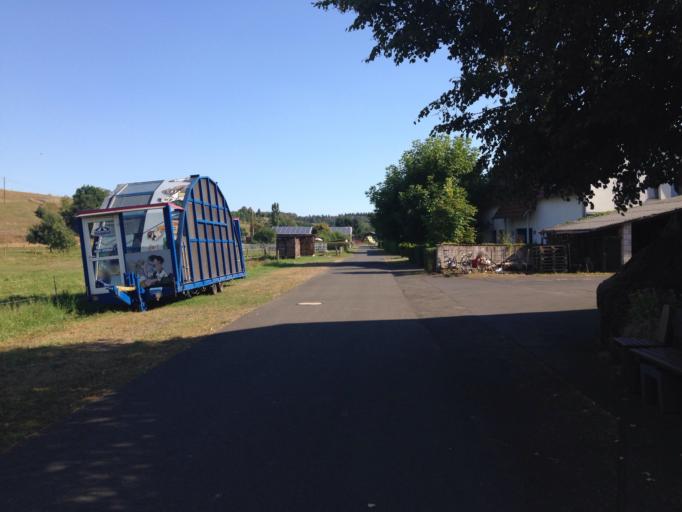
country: DE
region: Hesse
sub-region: Regierungsbezirk Giessen
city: Rabenau
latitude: 50.6491
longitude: 8.8952
